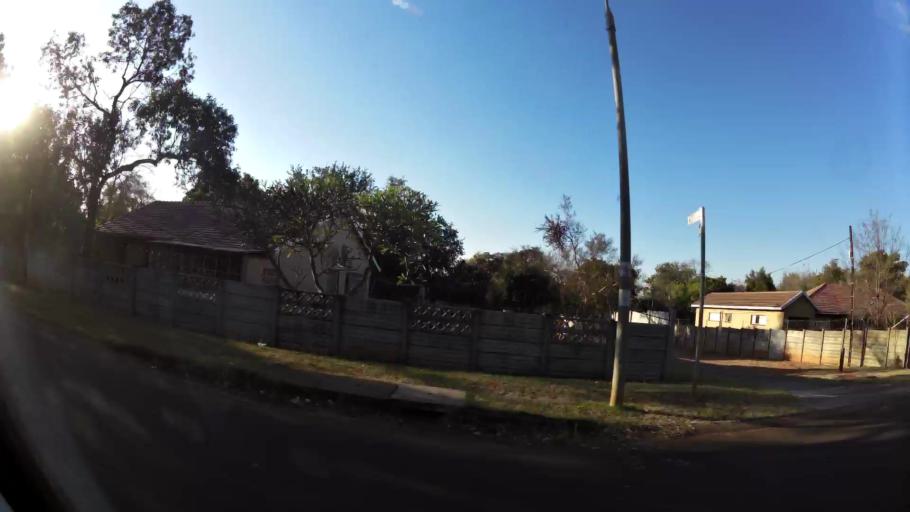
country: ZA
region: North-West
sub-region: Bojanala Platinum District Municipality
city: Rustenburg
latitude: -25.6896
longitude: 27.2134
